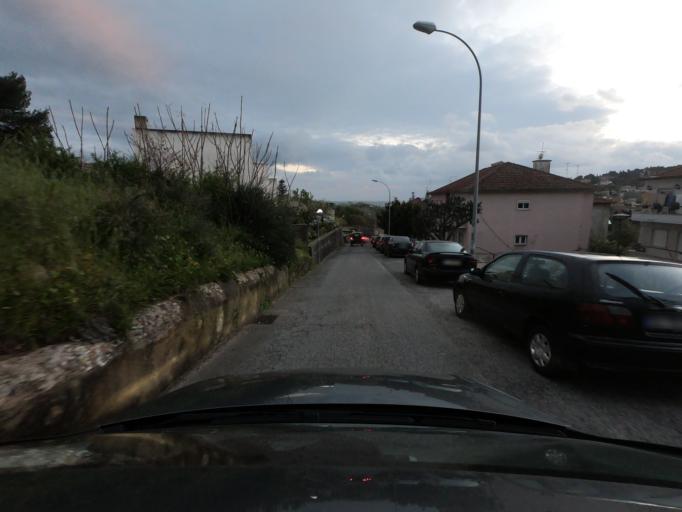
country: PT
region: Lisbon
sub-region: Oeiras
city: Terrugem
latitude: 38.7027
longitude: -9.2720
